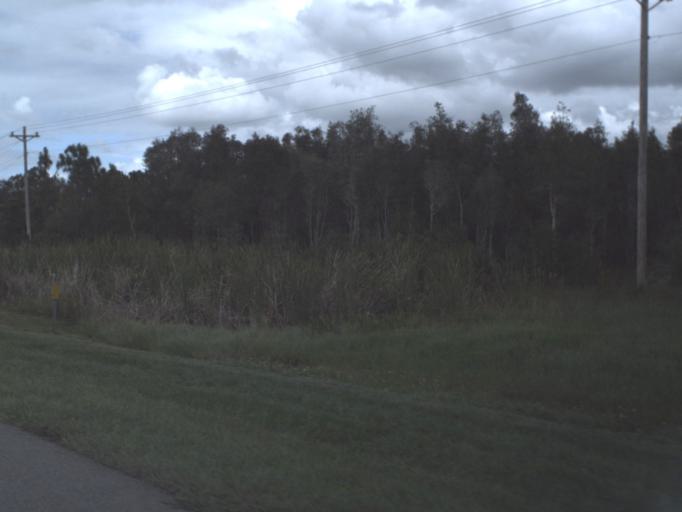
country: US
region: Florida
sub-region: Lee County
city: Lehigh Acres
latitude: 26.5347
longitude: -81.6276
